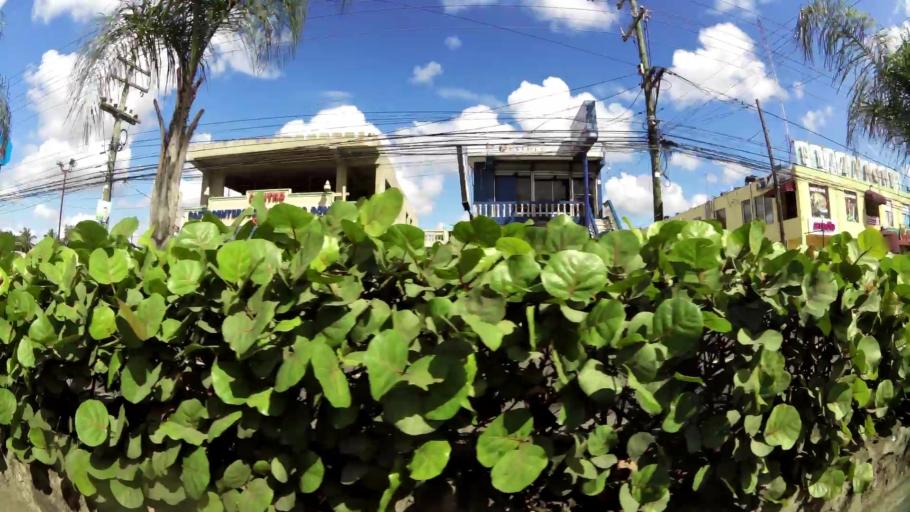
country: DO
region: Santo Domingo
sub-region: Santo Domingo
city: Santo Domingo Este
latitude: 18.5179
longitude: -69.8369
